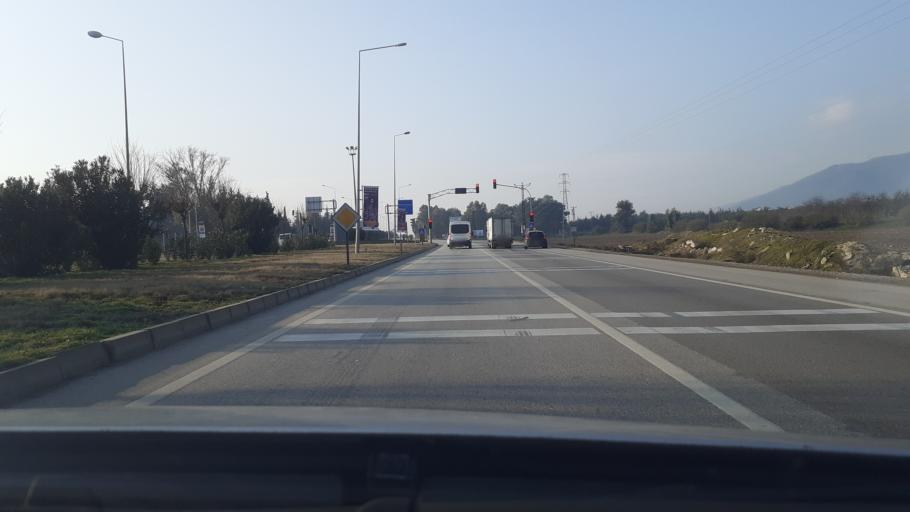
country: TR
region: Hatay
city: Serinyol
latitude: 36.3734
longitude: 36.2261
